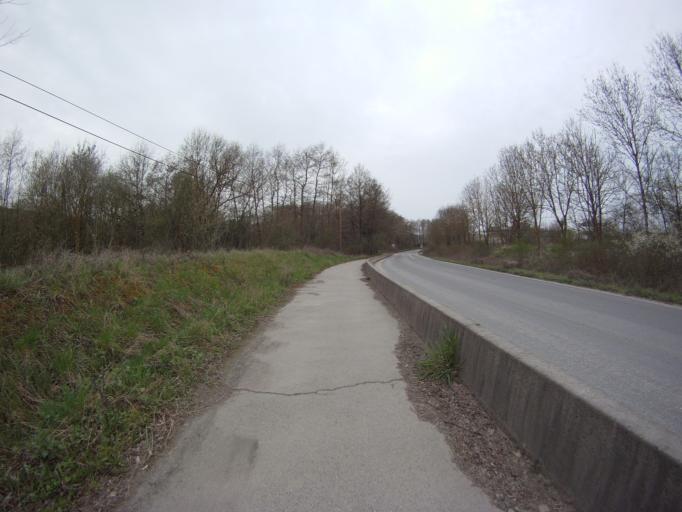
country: FR
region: Lorraine
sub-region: Departement de Meurthe-et-Moselle
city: Pont-Saint-Vincent
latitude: 48.6045
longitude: 6.1088
